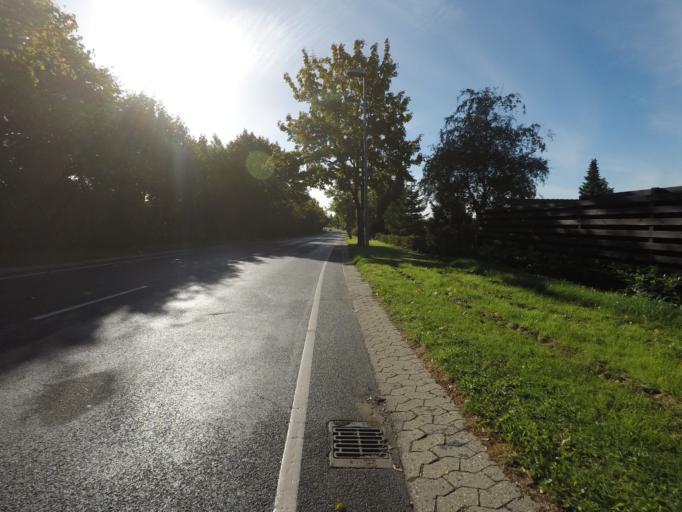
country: DK
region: Capital Region
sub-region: Egedal Kommune
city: Smorumnedre
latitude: 55.7407
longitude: 12.3005
